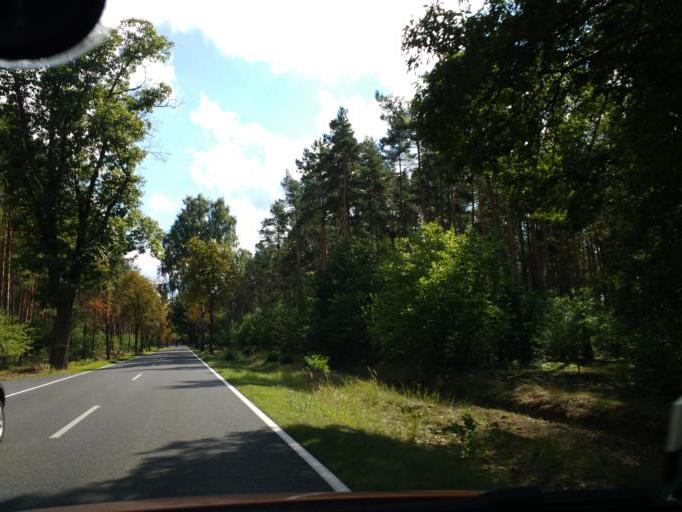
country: DE
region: Brandenburg
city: Birkenwerder
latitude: 52.7315
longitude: 13.3006
